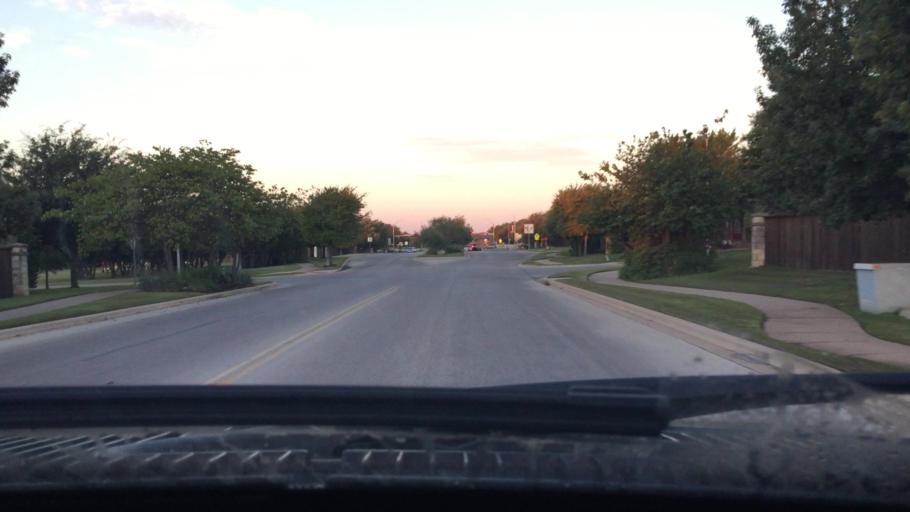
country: US
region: Texas
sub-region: Williamson County
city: Leander
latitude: 30.5391
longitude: -97.8586
